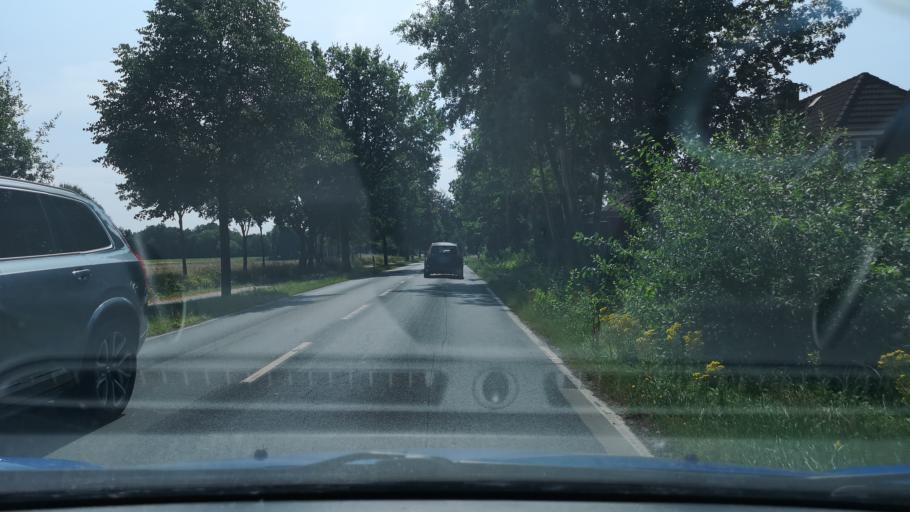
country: DE
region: Lower Saxony
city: Isernhagen Farster Bauerschaft
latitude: 52.4422
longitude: 9.8006
